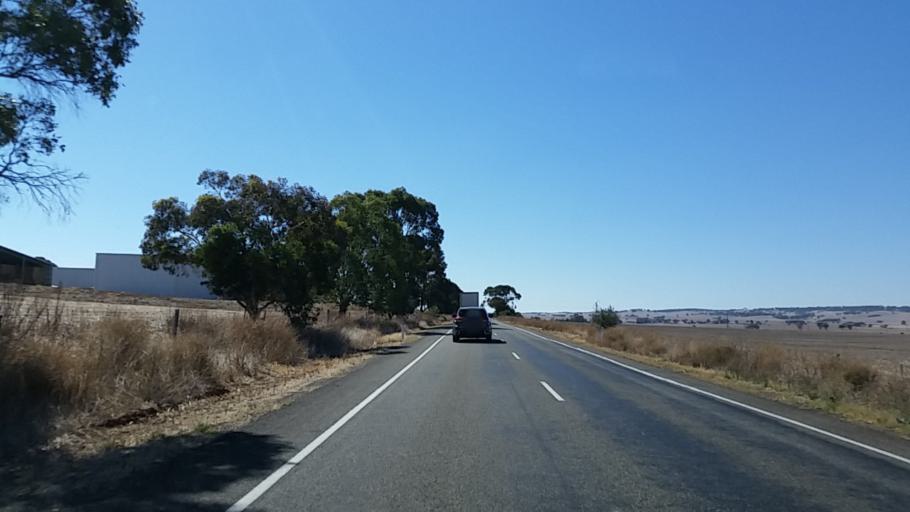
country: AU
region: South Australia
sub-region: Clare and Gilbert Valleys
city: Clare
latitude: -34.0252
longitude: 138.8047
